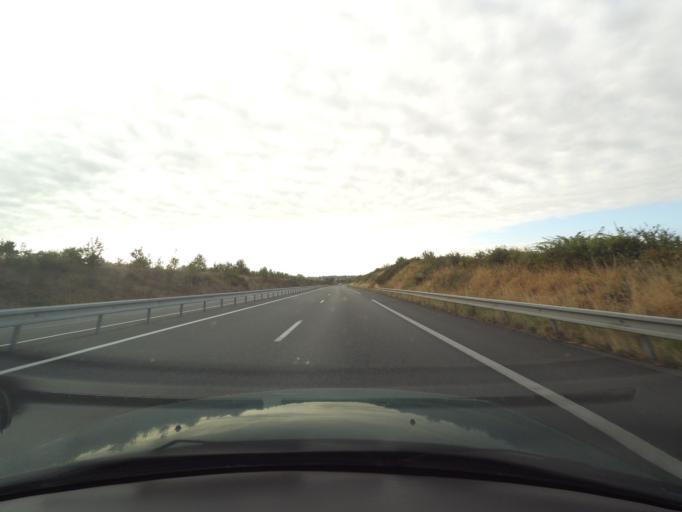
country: FR
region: Poitou-Charentes
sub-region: Departement des Deux-Sevres
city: Saint-Pierre-des-Echaubrognes
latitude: 46.9645
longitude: -0.7940
